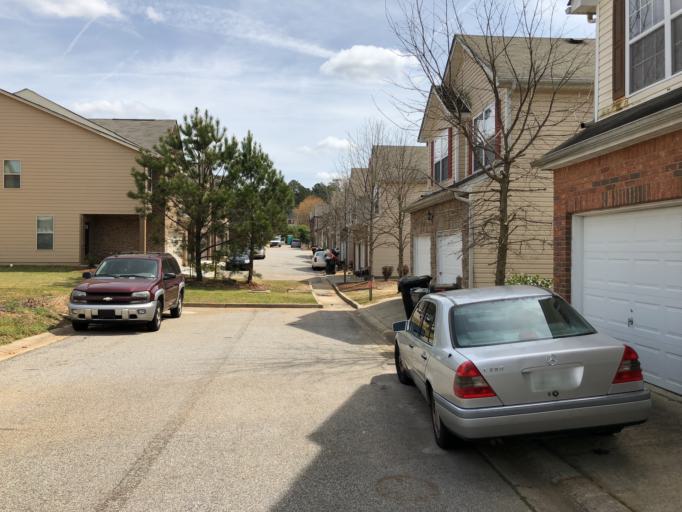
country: US
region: Georgia
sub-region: Clayton County
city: Riverdale
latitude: 33.6043
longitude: -84.4452
